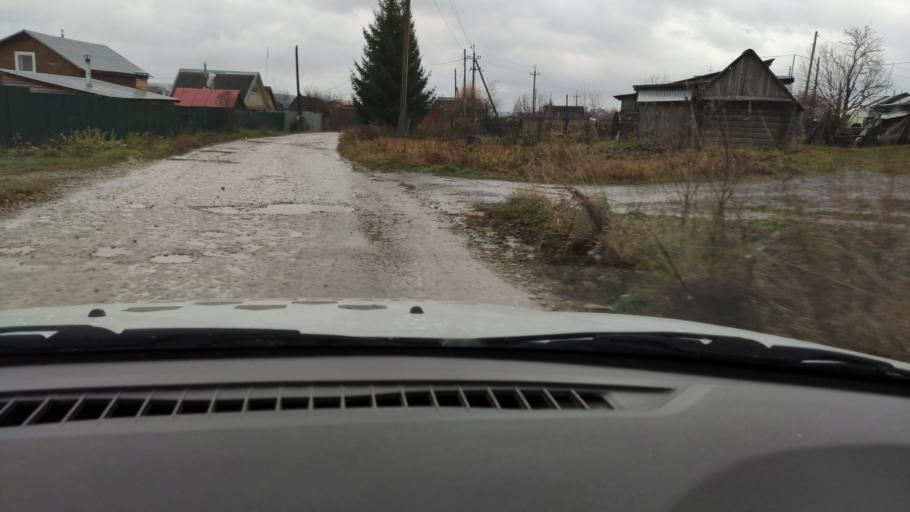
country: RU
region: Perm
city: Sylva
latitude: 58.0448
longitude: 56.7441
